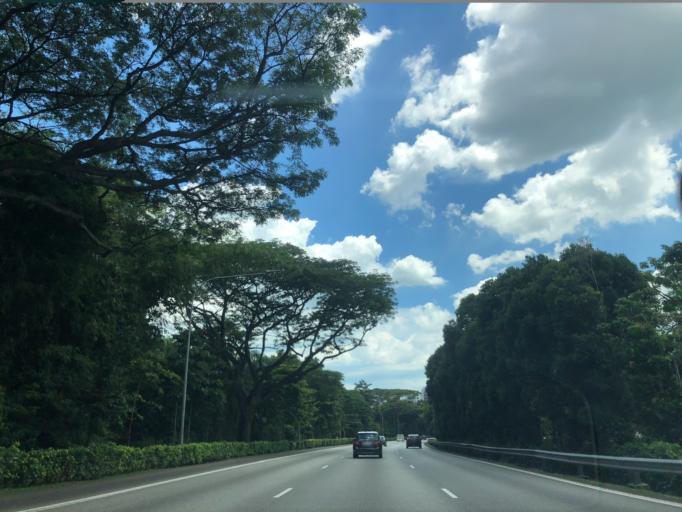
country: SG
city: Singapore
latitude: 1.2834
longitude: 103.8123
